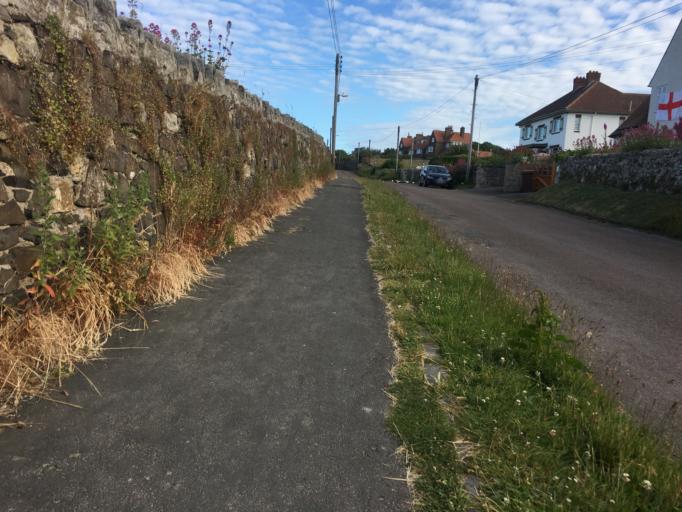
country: GB
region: England
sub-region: Northumberland
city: Bamburgh
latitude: 55.6104
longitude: -1.7165
